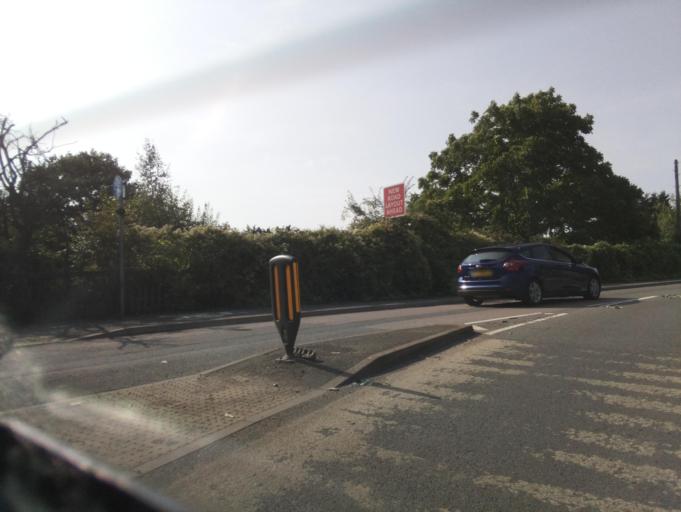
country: GB
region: England
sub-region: Staffordshire
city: Lichfield
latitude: 52.6882
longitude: -1.8011
